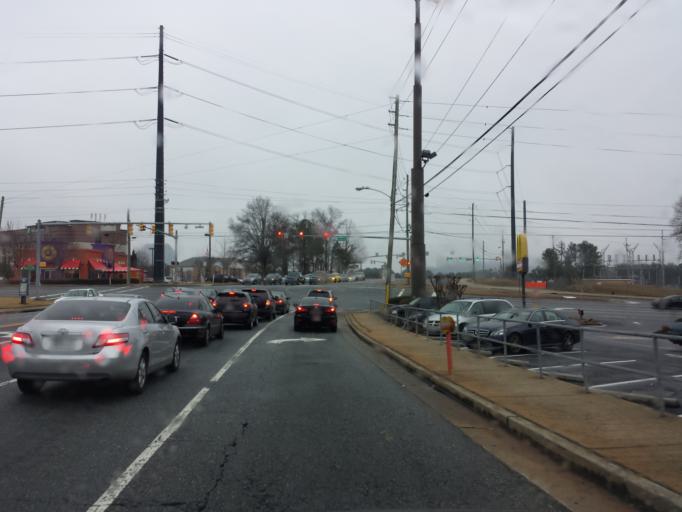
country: US
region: Georgia
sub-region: Cobb County
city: Vinings
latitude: 33.8840
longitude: -84.4763
